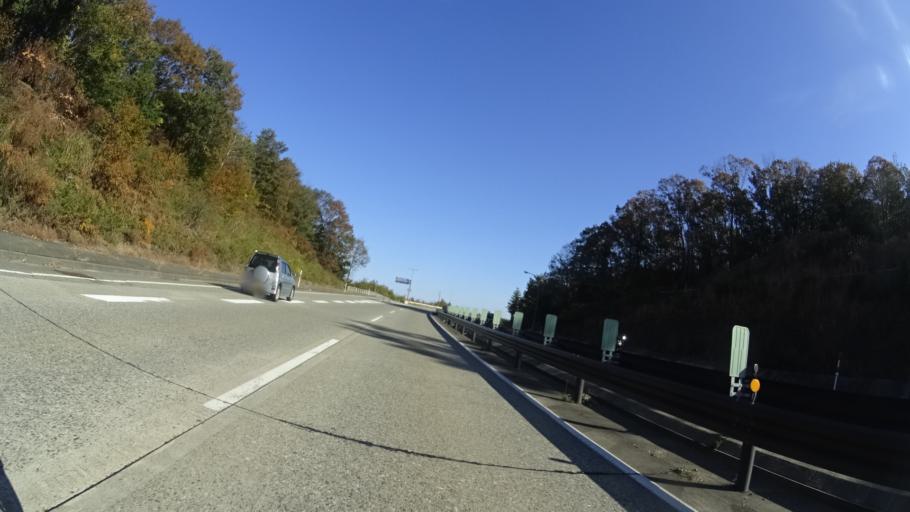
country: JP
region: Ishikawa
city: Komatsu
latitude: 36.3678
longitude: 136.4622
